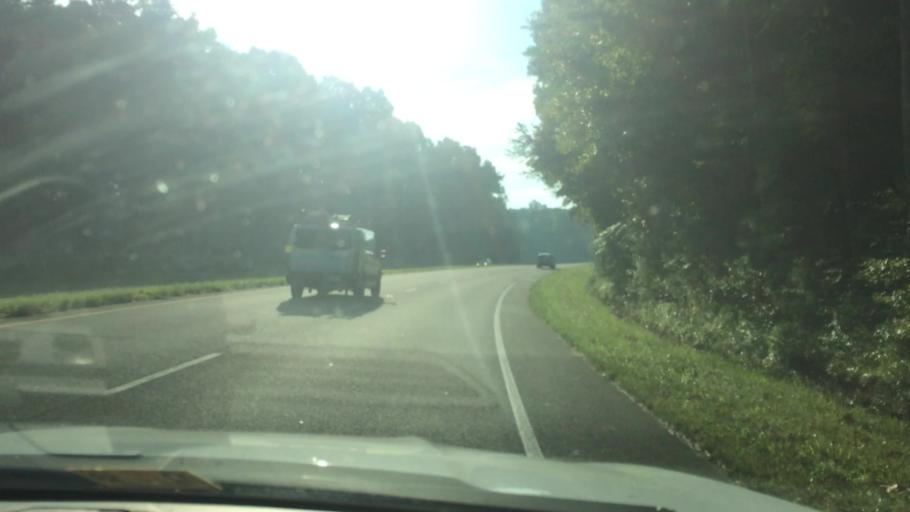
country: US
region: Virginia
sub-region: Gloucester County
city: Gloucester Courthouse
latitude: 37.4258
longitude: -76.4921
